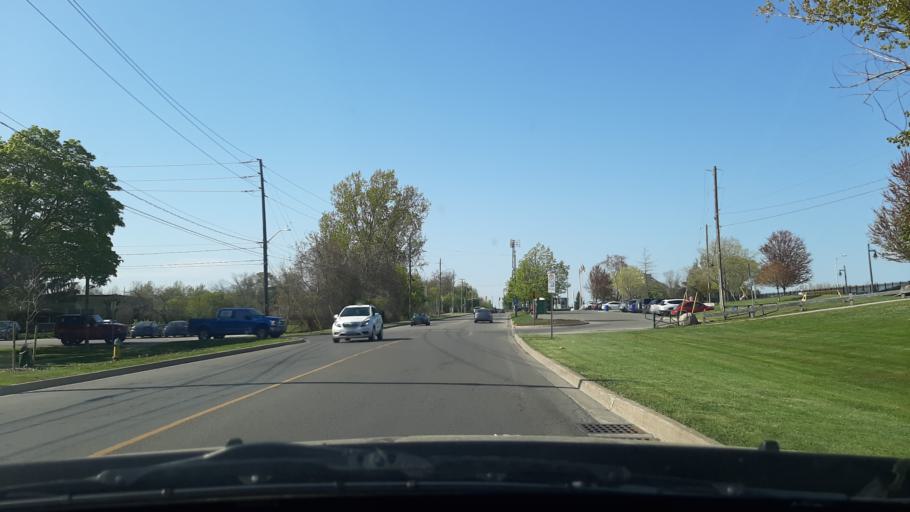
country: CA
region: Ontario
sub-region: Regional Municipality of Niagara
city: St. Catharines
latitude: 43.2103
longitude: -79.2119
